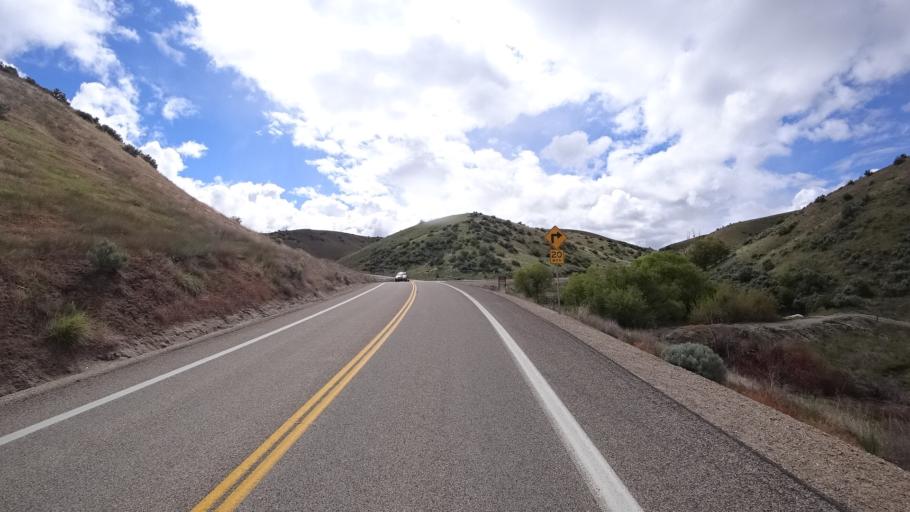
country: US
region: Idaho
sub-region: Ada County
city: Garden City
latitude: 43.6995
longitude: -116.2297
